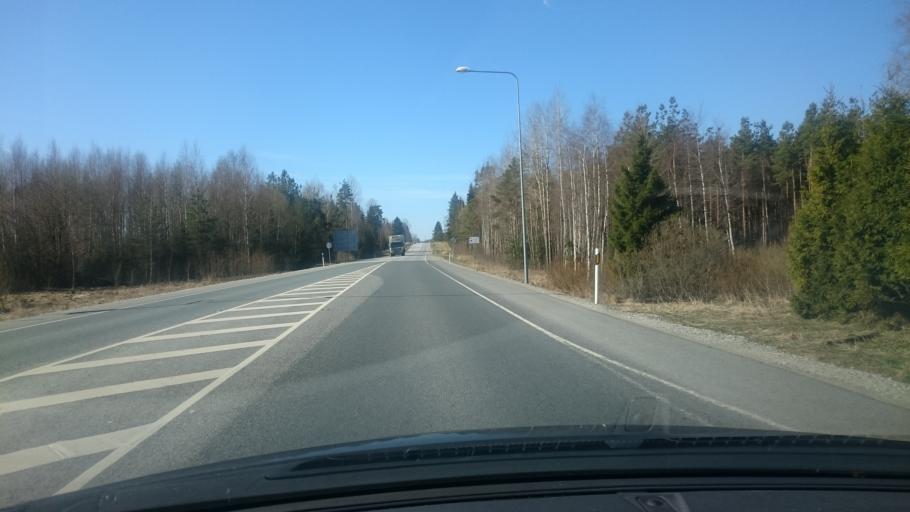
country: EE
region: Raplamaa
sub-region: Rapla vald
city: Rapla
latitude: 59.0392
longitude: 24.8355
